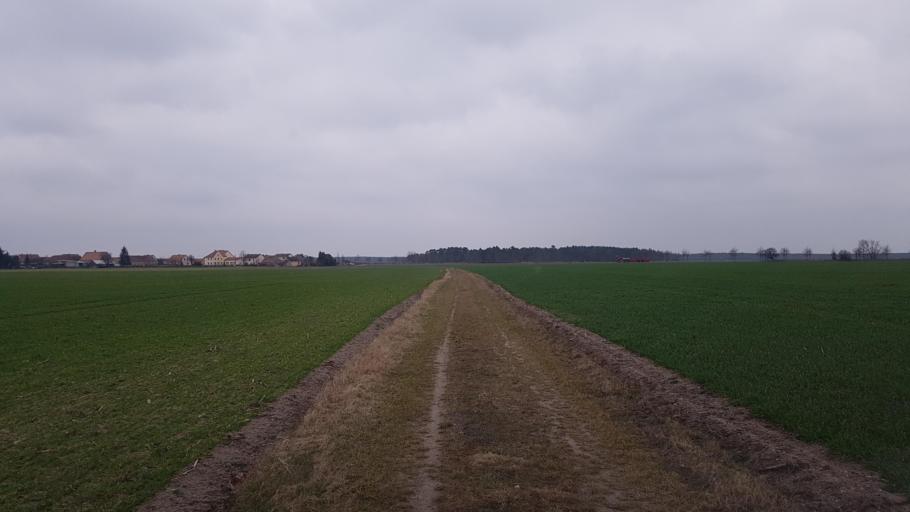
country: DE
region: Saxony
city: Nauwalde
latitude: 51.4358
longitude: 13.3610
